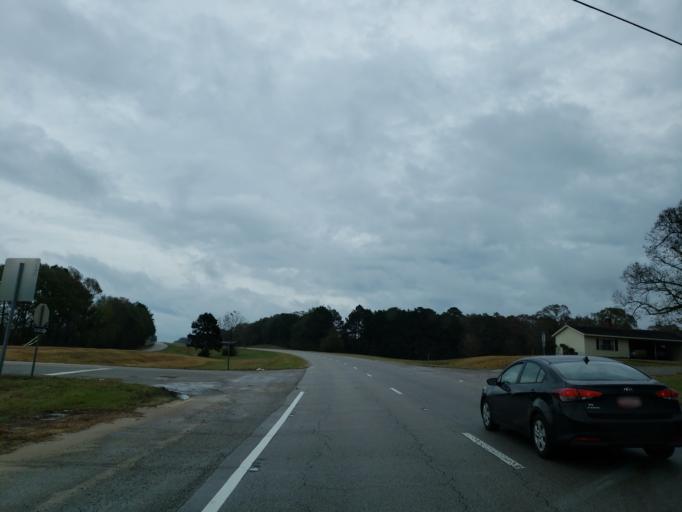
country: US
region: Mississippi
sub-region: Jones County
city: Sharon
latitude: 31.6972
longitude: -88.8938
